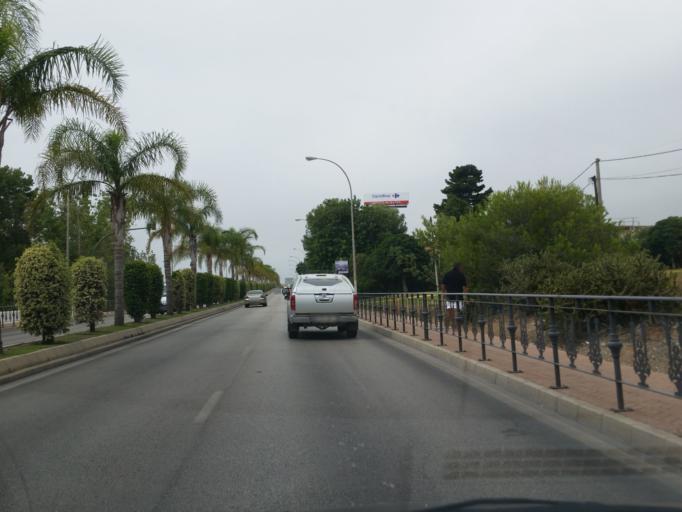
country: ES
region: Andalusia
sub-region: Provincia de Malaga
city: Torremolinos
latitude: 36.6145
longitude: -4.5106
